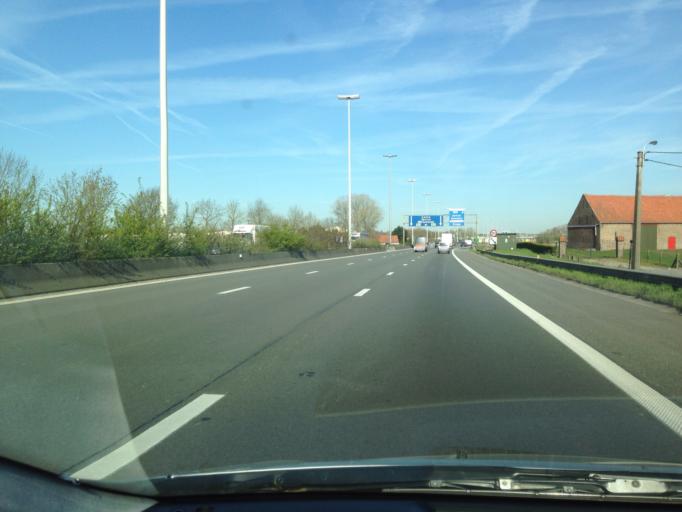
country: BE
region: Flanders
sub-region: Provincie West-Vlaanderen
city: Oostkamp
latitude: 51.1497
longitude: 3.2236
